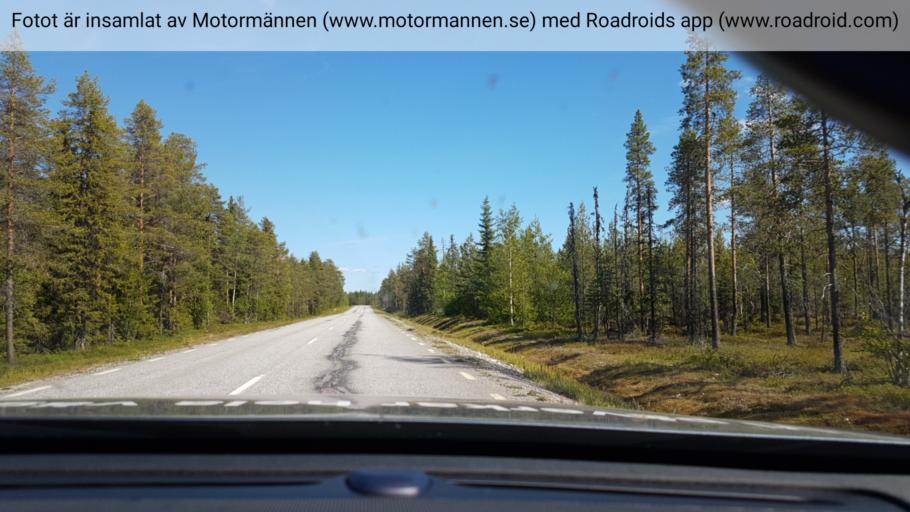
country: SE
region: Vaesterbotten
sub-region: Lycksele Kommun
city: Soderfors
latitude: 64.6242
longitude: 18.0953
